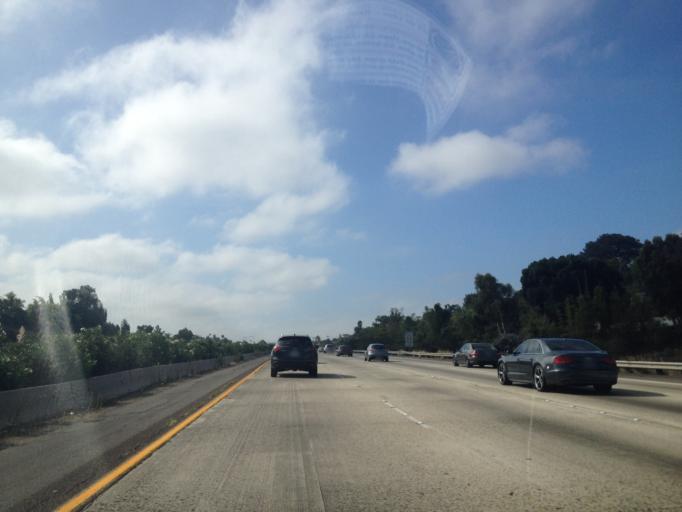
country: US
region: California
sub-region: San Diego County
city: Encinitas
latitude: 33.0732
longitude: -117.2948
